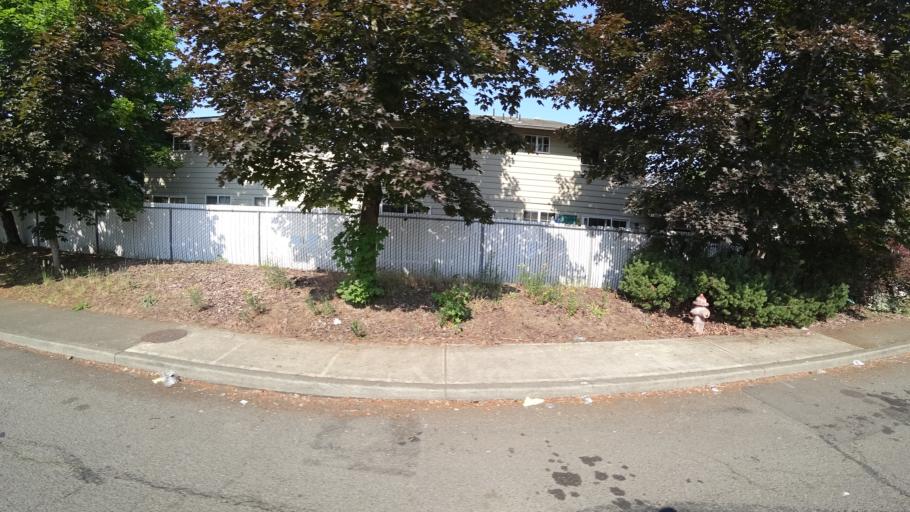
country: US
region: Oregon
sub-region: Multnomah County
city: Lents
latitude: 45.4578
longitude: -122.5821
